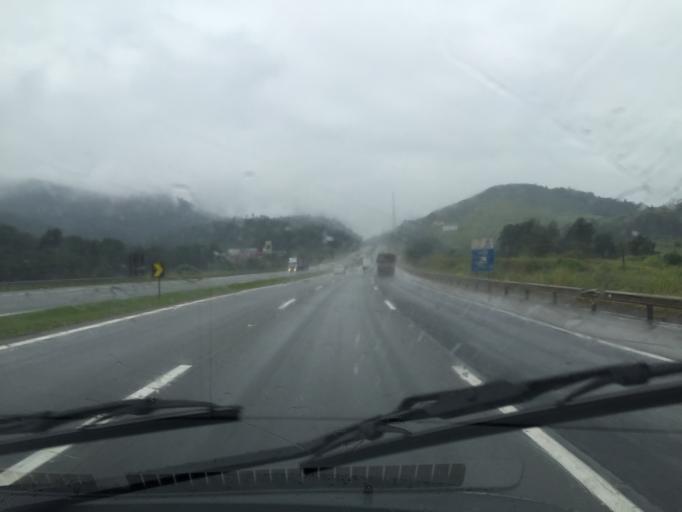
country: BR
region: Sao Paulo
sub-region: Sao Roque
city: Sao Roque
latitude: -23.4300
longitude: -47.1293
